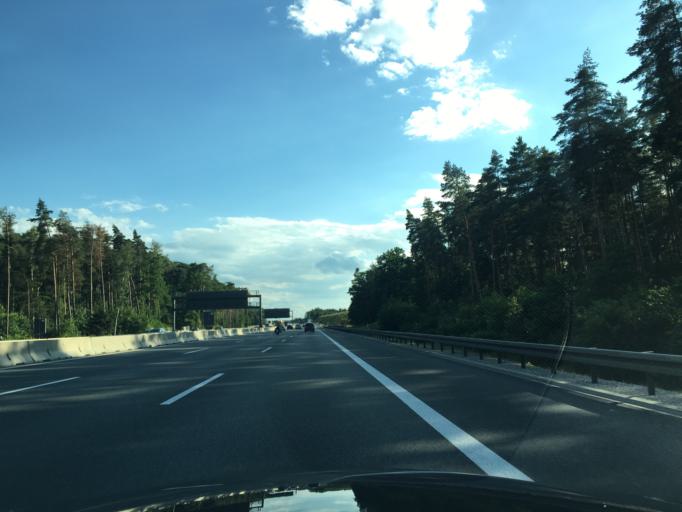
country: DE
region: Bavaria
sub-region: Regierungsbezirk Mittelfranken
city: Wendelstein
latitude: 49.3641
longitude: 11.1181
